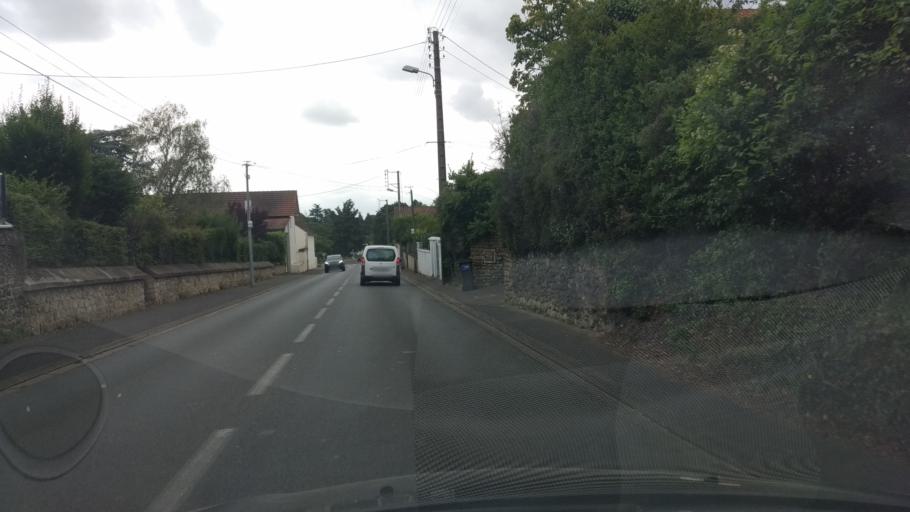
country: FR
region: Poitou-Charentes
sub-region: Departement de la Vienne
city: Saint-Benoit
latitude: 46.5605
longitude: 0.3555
